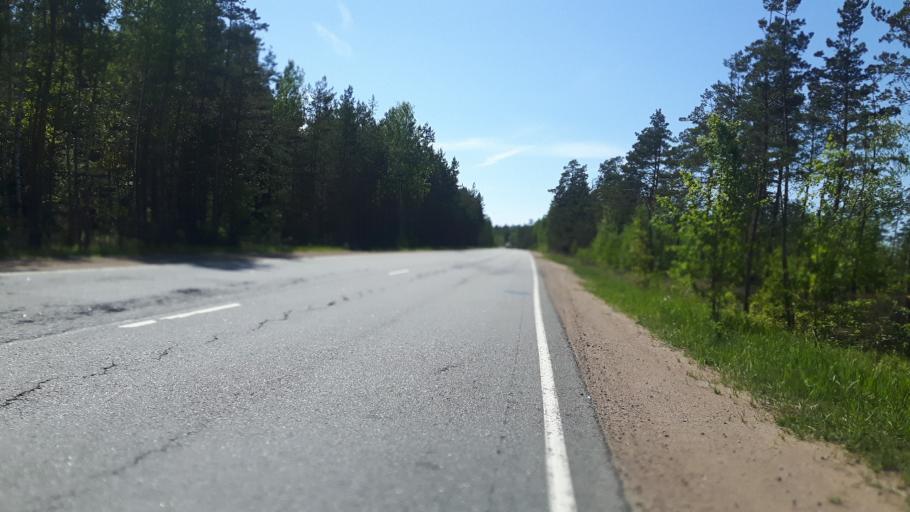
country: RU
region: Leningrad
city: Sista-Palkino
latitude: 59.7694
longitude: 28.7720
